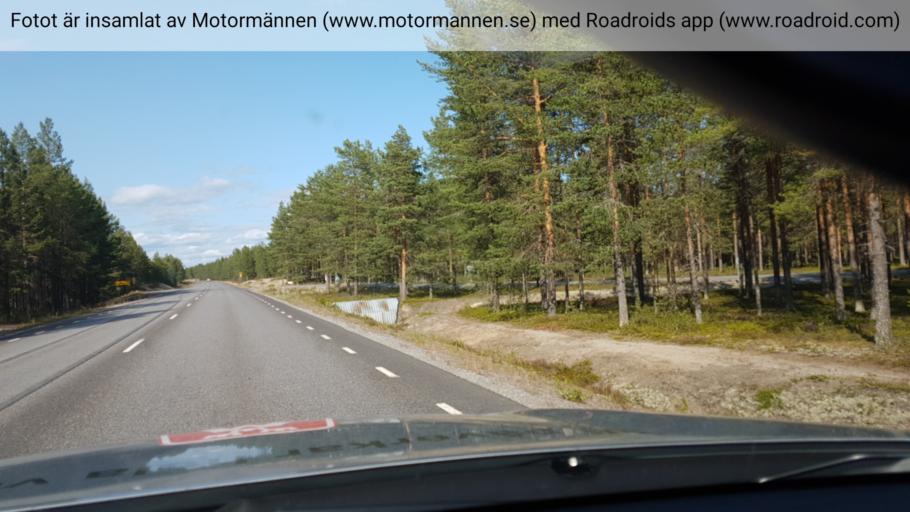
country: SE
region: Norrbotten
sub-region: Pitea Kommun
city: Pitea
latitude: 65.2479
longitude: 21.5346
